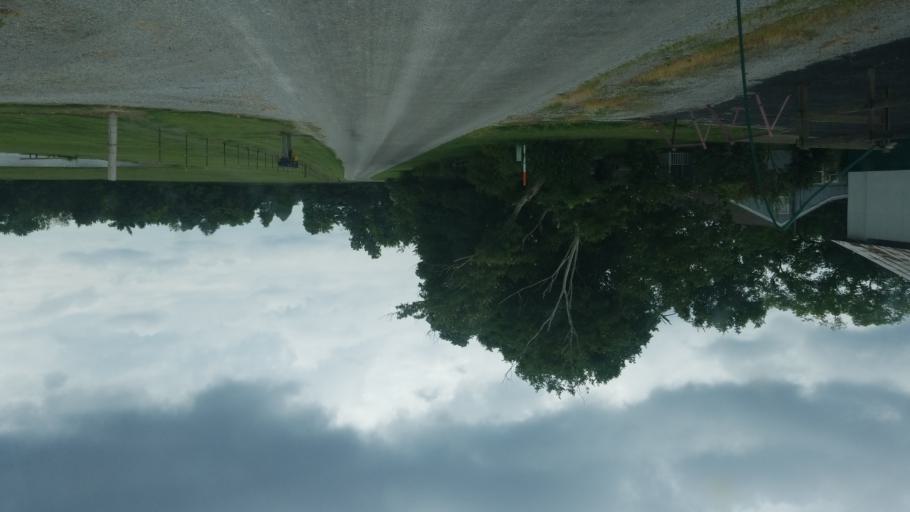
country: US
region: Illinois
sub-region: Jackson County
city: Murphysboro
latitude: 37.7150
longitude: -89.3280
